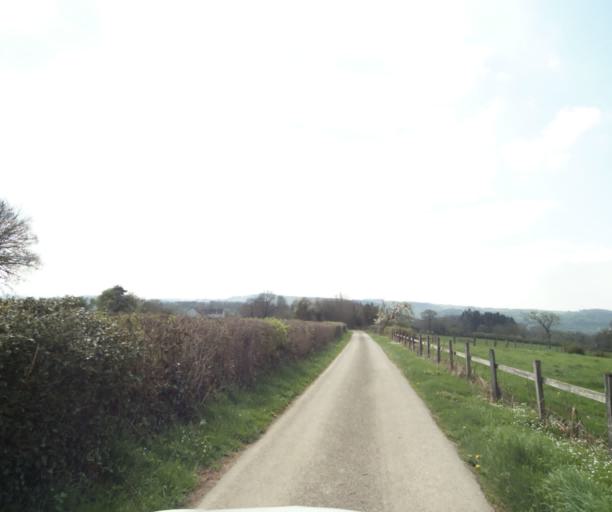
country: FR
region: Bourgogne
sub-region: Departement de Saone-et-Loire
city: Charolles
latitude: 46.3761
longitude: 4.3073
